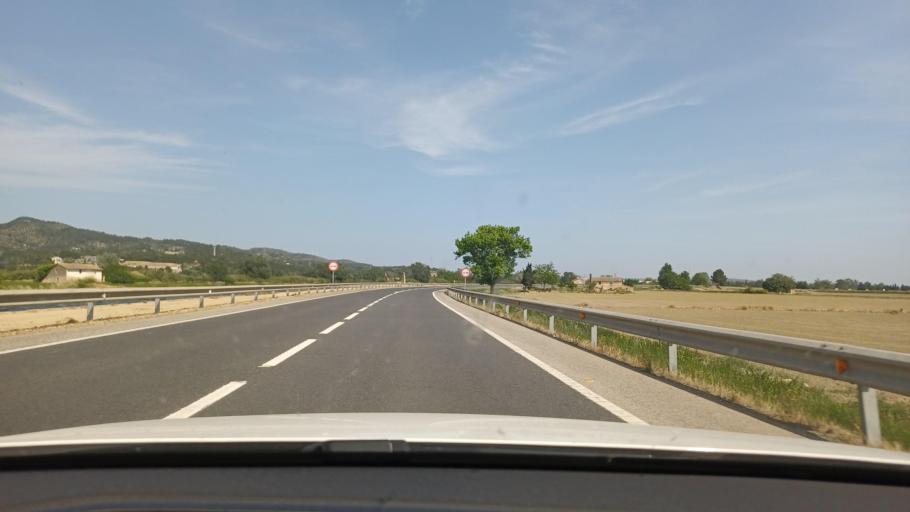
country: ES
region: Catalonia
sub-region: Provincia de Tarragona
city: Tortosa
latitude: 40.7754
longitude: 0.5227
